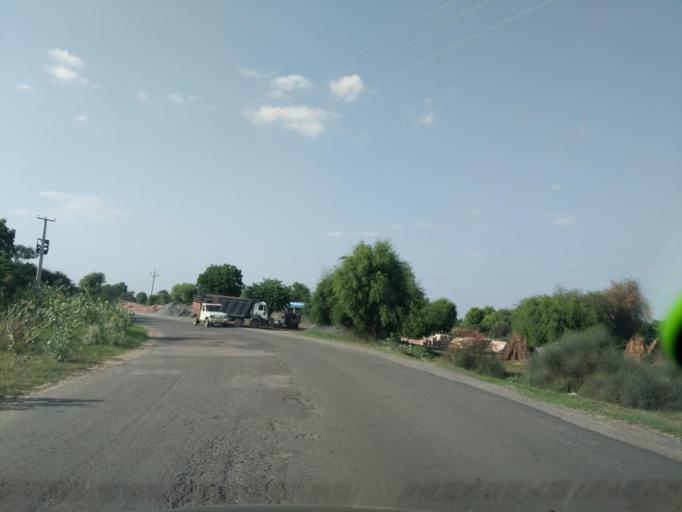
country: IN
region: Rajasthan
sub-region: Churu
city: Rajgarh
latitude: 28.5196
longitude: 75.3833
